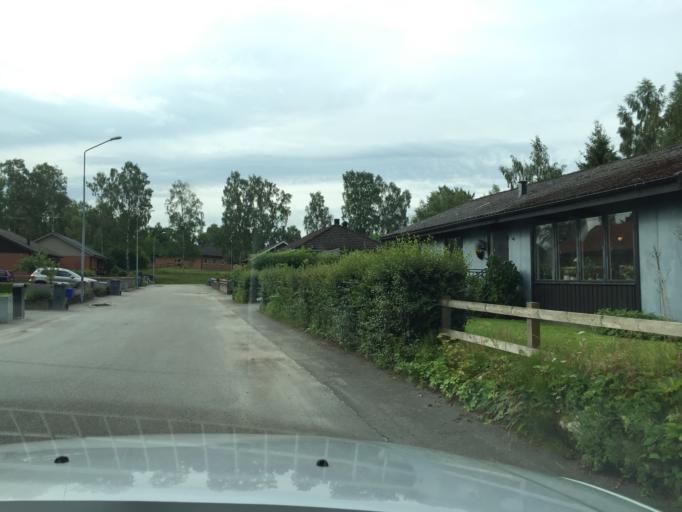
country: SE
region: Skane
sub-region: Hassleholms Kommun
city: Sosdala
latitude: 56.0436
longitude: 13.6762
